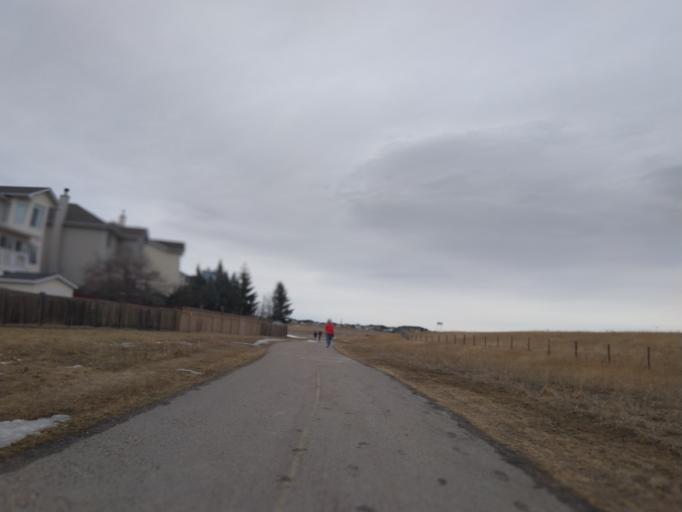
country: CA
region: Alberta
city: Chestermere
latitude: 51.1083
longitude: -113.9227
